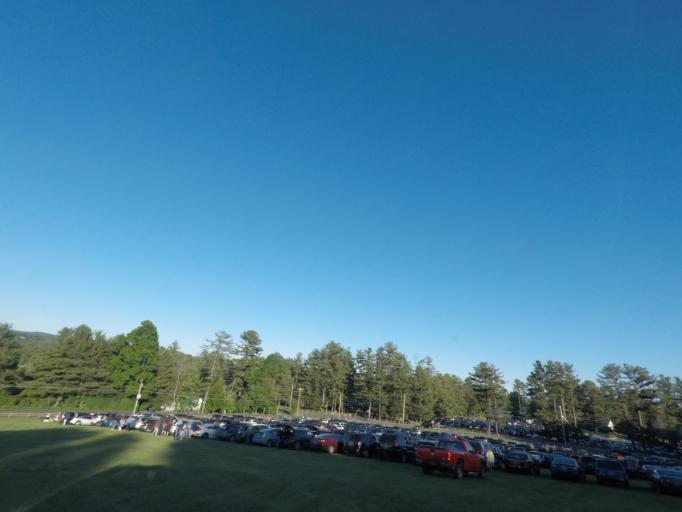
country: US
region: Massachusetts
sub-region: Berkshire County
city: Lenox
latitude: 42.3534
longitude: -73.3131
